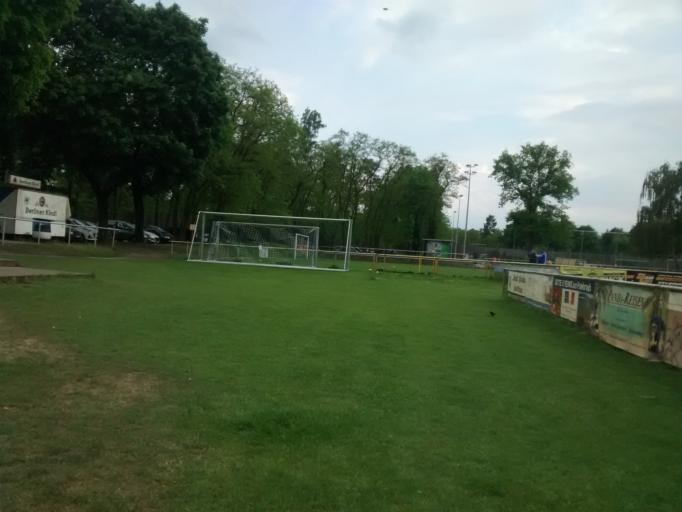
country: DE
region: Brandenburg
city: Hohen Neuendorf
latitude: 52.6786
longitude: 13.2616
